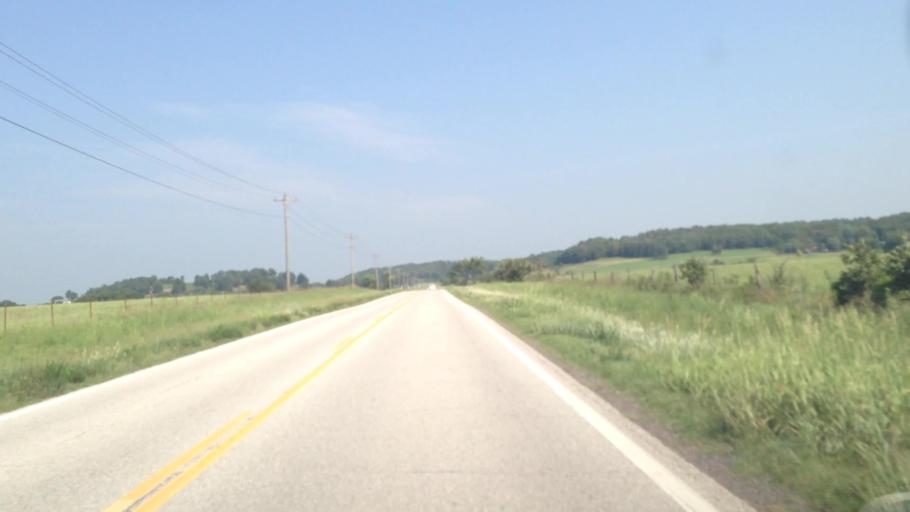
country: US
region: Oklahoma
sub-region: Craig County
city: Vinita
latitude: 36.7633
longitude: -95.1435
